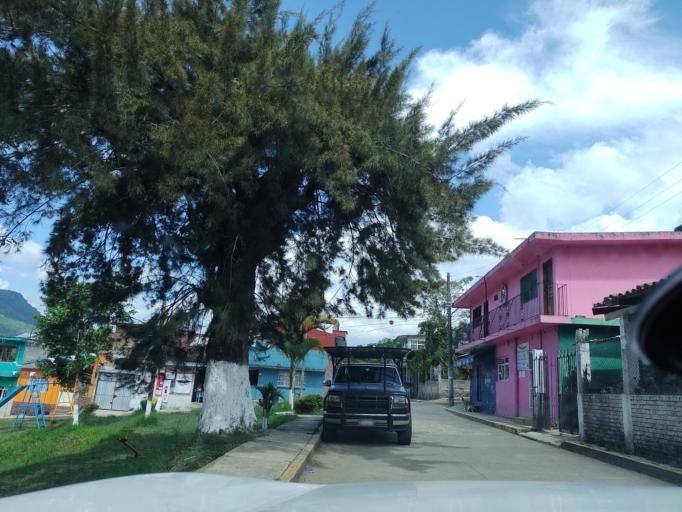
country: MX
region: Veracruz
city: Coatepec
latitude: 19.4299
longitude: -96.9645
